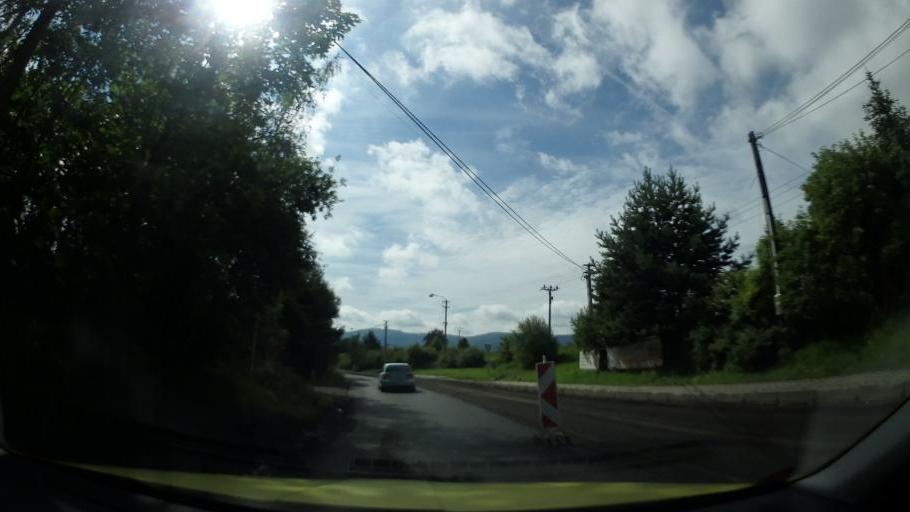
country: CZ
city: Hodslavice
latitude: 49.5543
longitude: 18.0220
